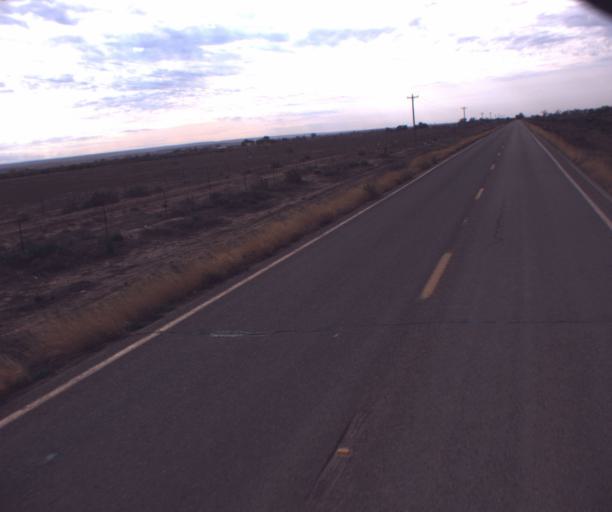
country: US
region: Arizona
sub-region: Apache County
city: Many Farms
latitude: 36.4320
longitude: -109.6068
